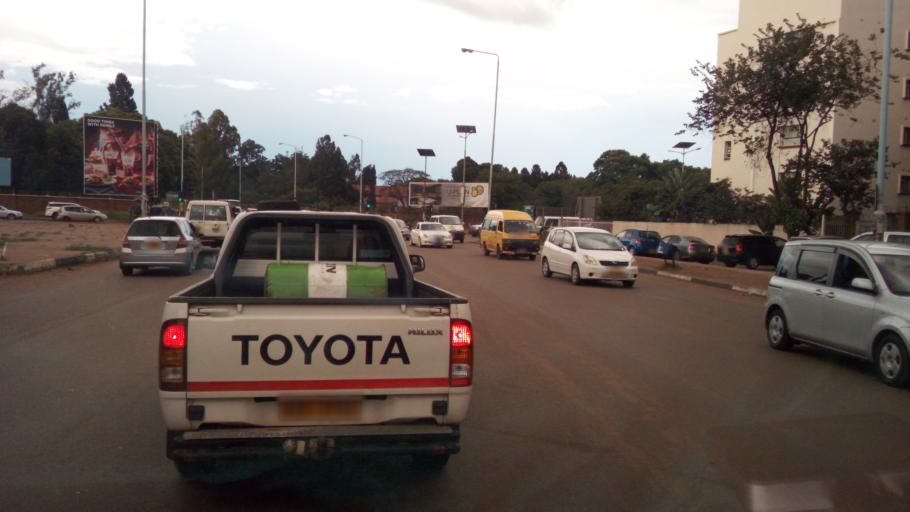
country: ZW
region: Harare
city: Harare
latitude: -17.8295
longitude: 31.0400
